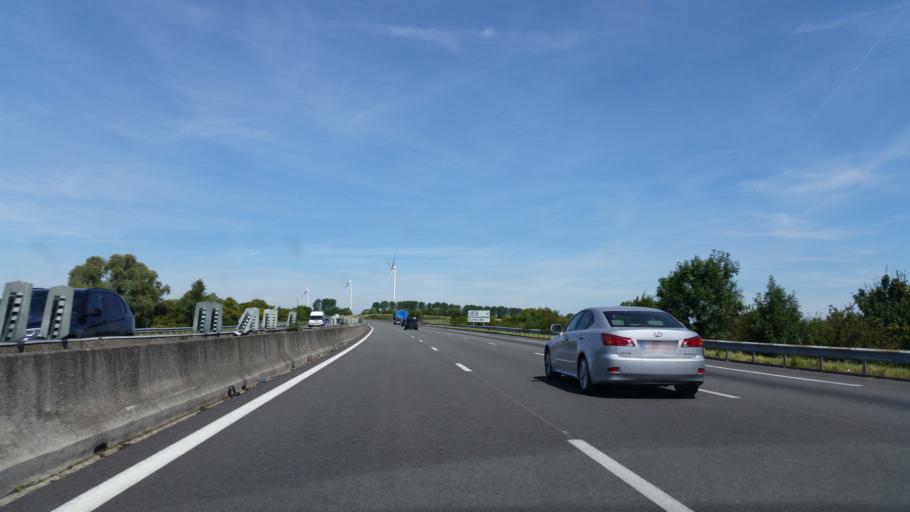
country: FR
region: Picardie
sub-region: Departement de la Somme
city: Moislains
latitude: 50.0201
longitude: 2.8831
